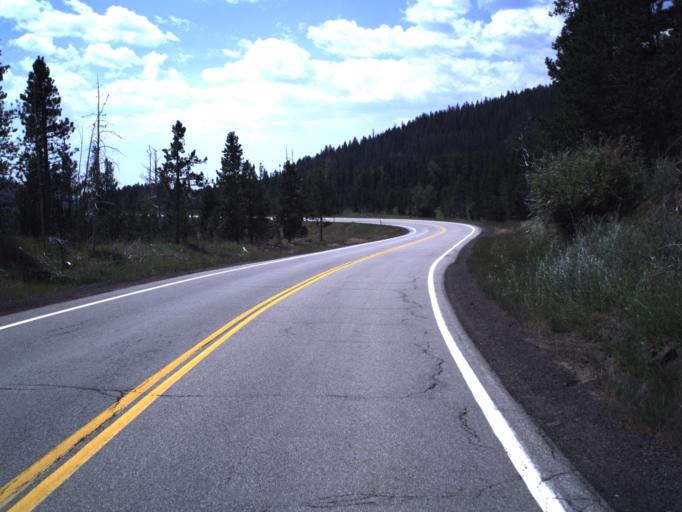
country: US
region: Utah
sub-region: Daggett County
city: Manila
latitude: 40.8333
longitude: -109.4626
